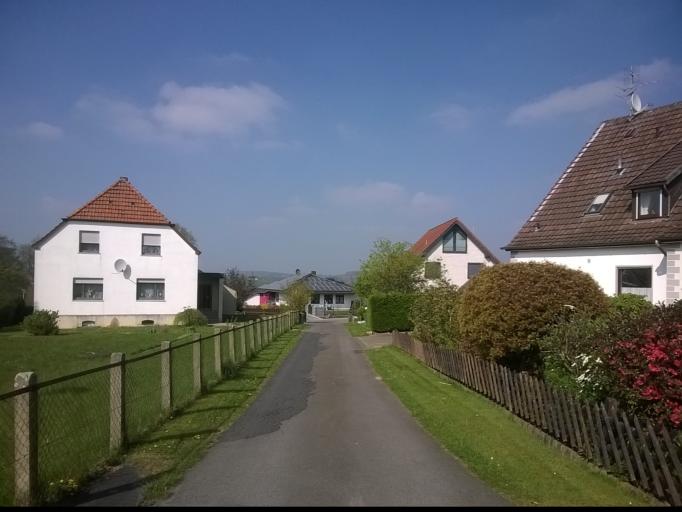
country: DE
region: North Rhine-Westphalia
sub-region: Regierungsbezirk Detmold
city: Hiddenhausen
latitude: 52.1326
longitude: 8.6242
